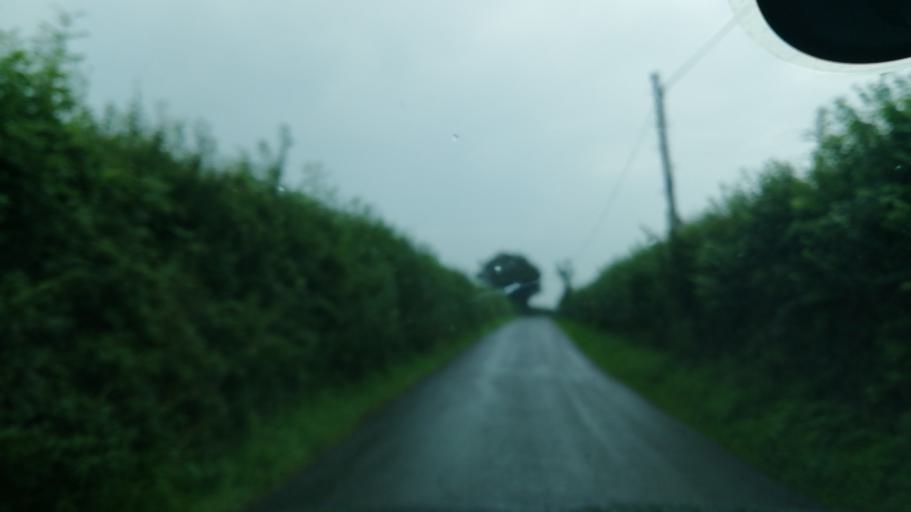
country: IE
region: Leinster
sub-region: Kilkenny
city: Callan
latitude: 52.5393
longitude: -7.3130
